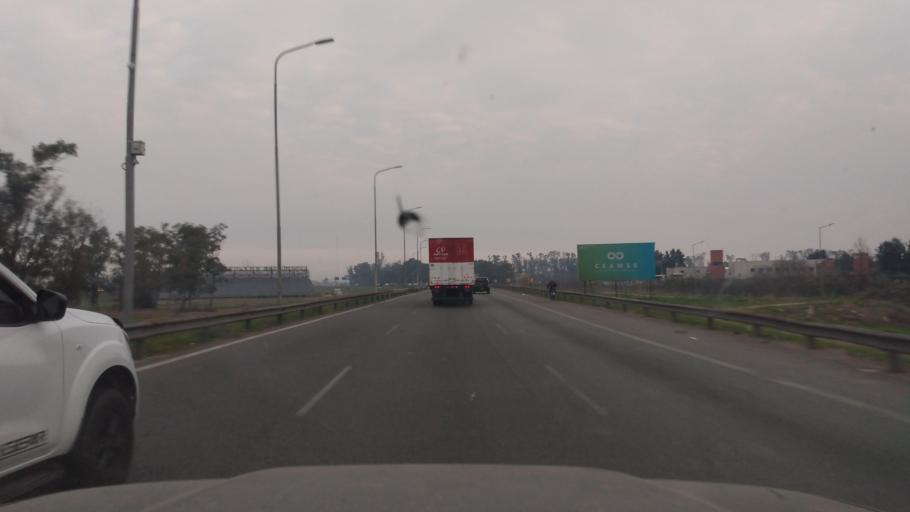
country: AR
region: Buenos Aires
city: Hurlingham
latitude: -34.5220
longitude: -58.5920
